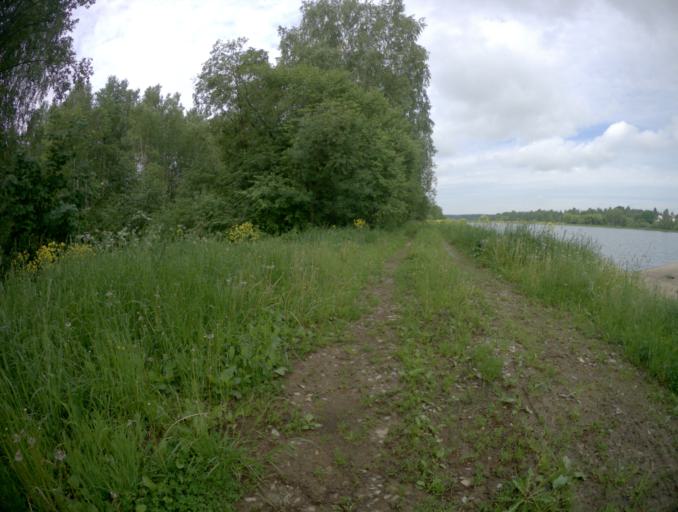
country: RU
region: Vladimir
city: Lakinsk
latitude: 56.0695
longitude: 39.9610
